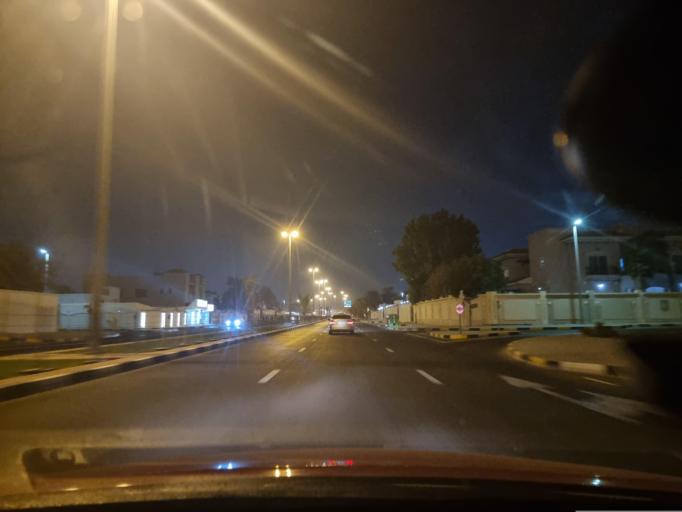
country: AE
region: Ash Shariqah
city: Sharjah
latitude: 25.3625
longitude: 55.4371
